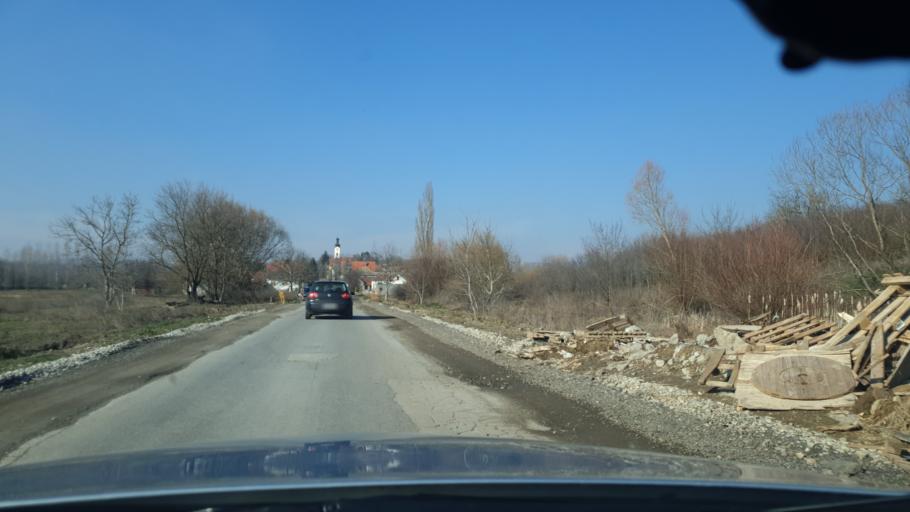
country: RS
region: Autonomna Pokrajina Vojvodina
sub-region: Sremski Okrug
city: Irig
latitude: 45.0847
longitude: 19.8384
